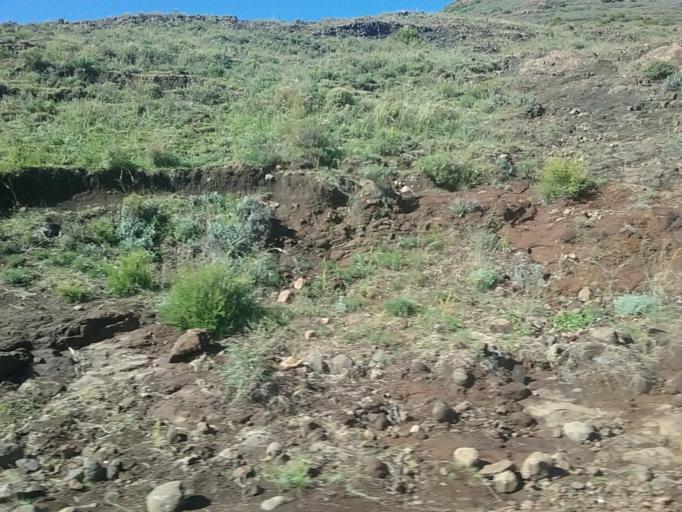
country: LS
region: Berea
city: Teyateyaneng
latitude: -29.2350
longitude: 27.9166
